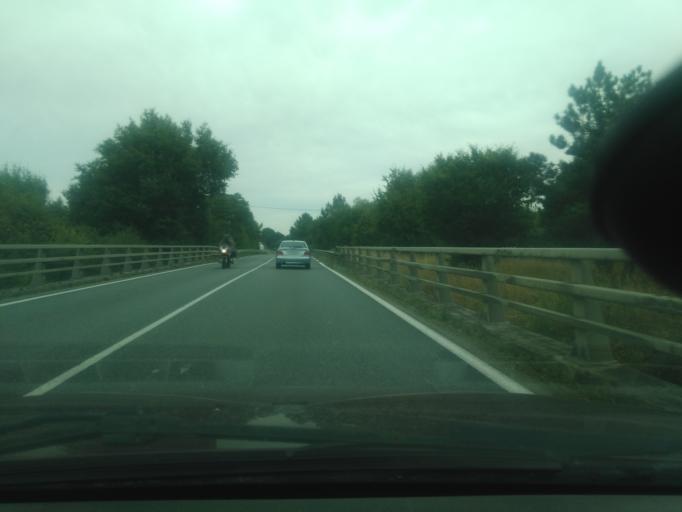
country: FR
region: Poitou-Charentes
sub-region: Departement des Deux-Sevres
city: Chatillon-sur-Thouet
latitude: 46.6485
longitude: -0.1904
